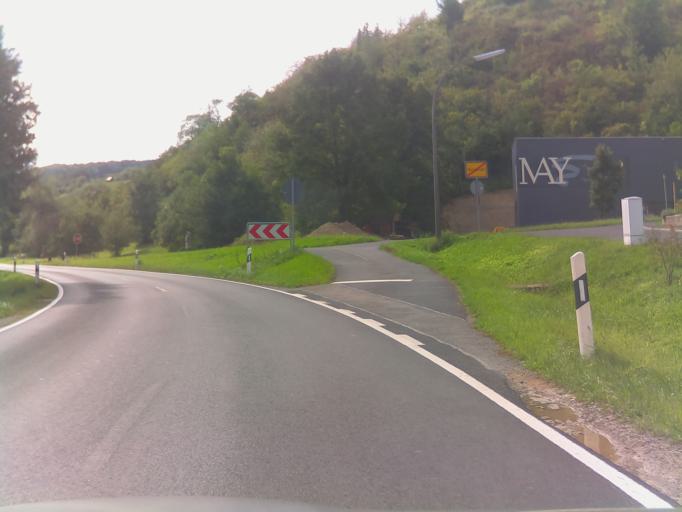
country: DE
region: Bavaria
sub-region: Regierungsbezirk Unterfranken
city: Retzstadt
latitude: 49.9123
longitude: 9.8690
